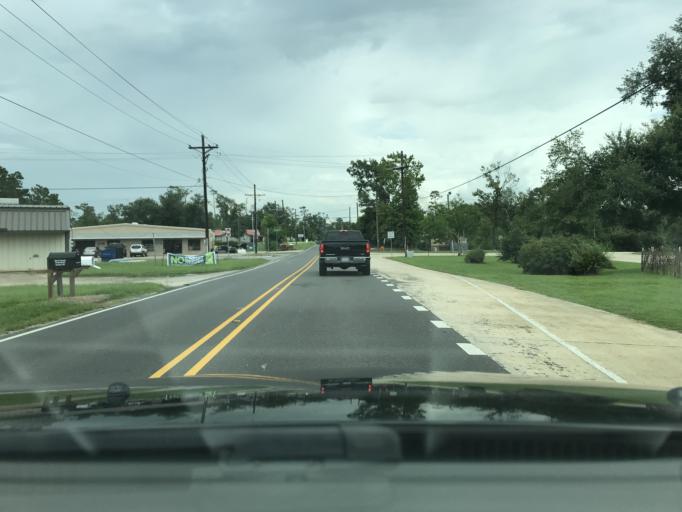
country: US
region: Louisiana
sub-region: Calcasieu Parish
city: Moss Bluff
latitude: 30.3007
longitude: -93.1901
